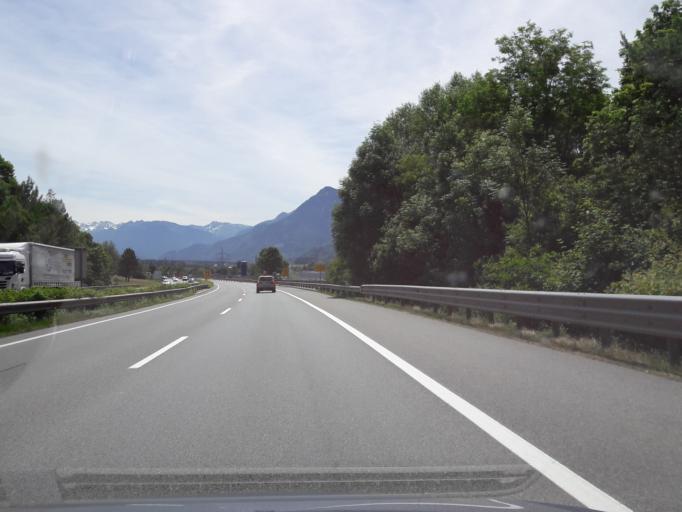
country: AT
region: Vorarlberg
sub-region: Politischer Bezirk Feldkirch
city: Gofis
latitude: 47.2289
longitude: 9.6186
